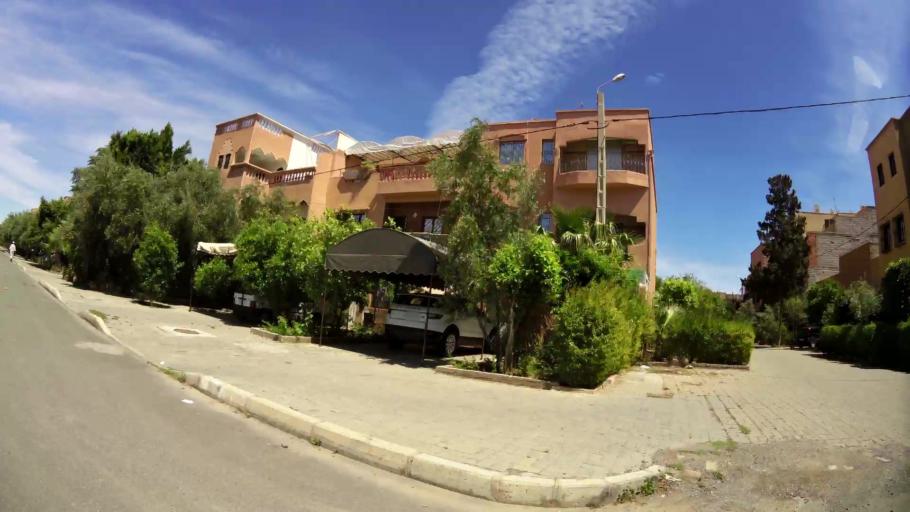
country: MA
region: Marrakech-Tensift-Al Haouz
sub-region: Marrakech
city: Marrakesh
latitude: 31.6415
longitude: -8.0562
